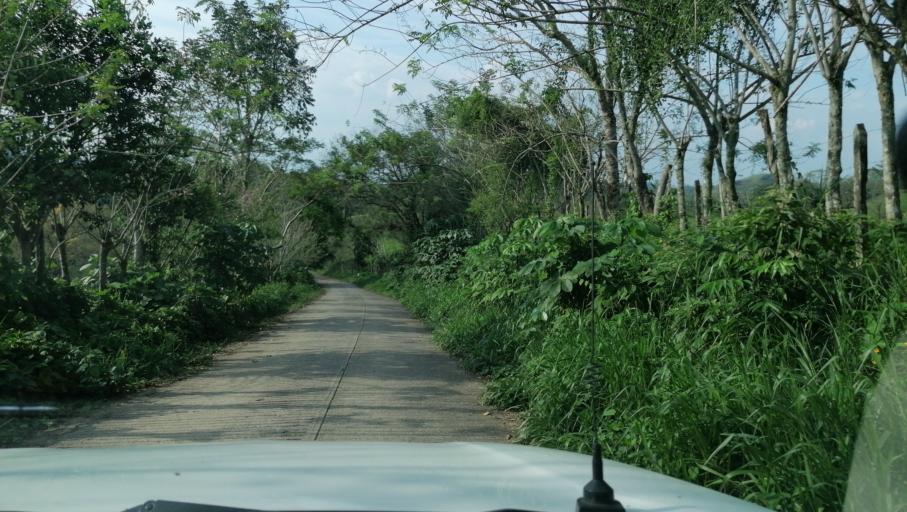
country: MX
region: Chiapas
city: Ostuacan
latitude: 17.4830
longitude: -93.2402
